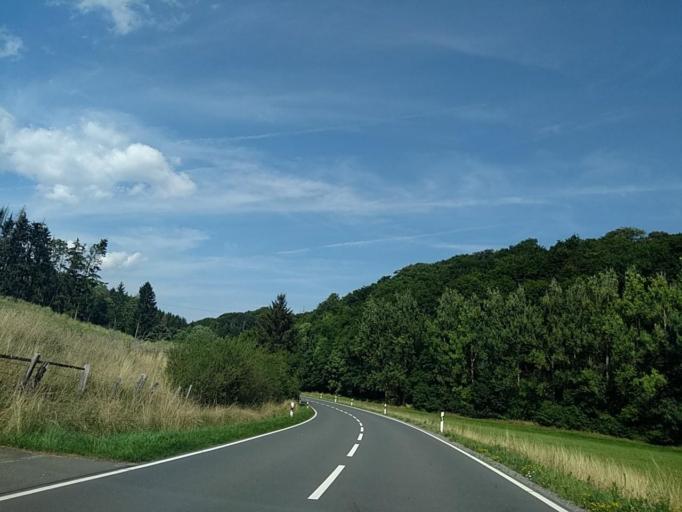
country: DE
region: North Rhine-Westphalia
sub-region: Regierungsbezirk Arnsberg
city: Brilon
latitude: 51.4426
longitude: 8.6393
